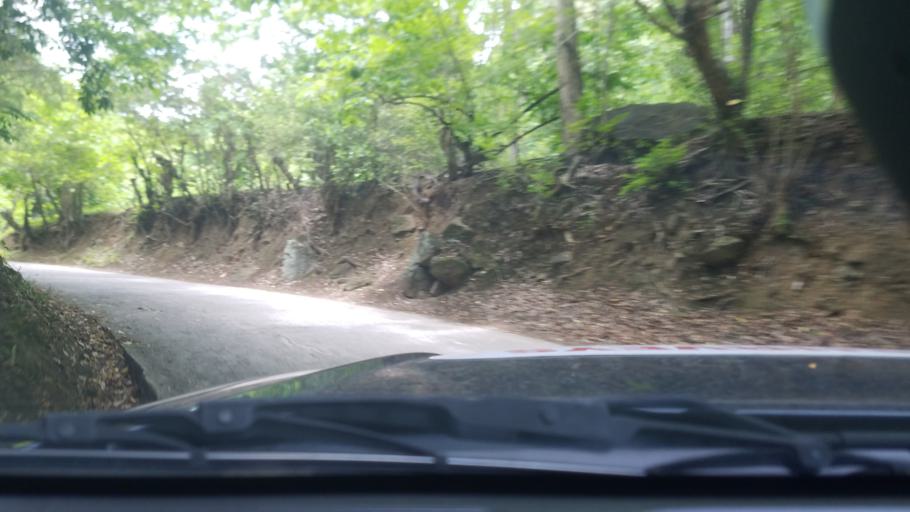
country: LC
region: Soufriere
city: Soufriere
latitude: 13.8390
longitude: -61.0618
